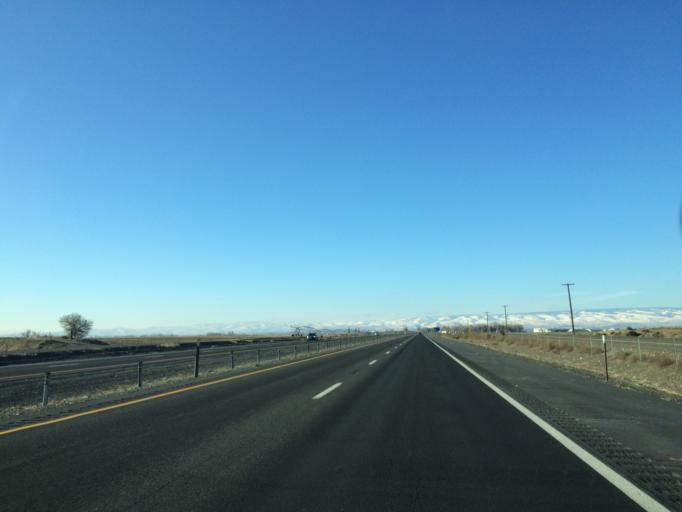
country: US
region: Washington
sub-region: Grant County
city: Quincy
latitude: 47.1035
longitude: -119.8126
